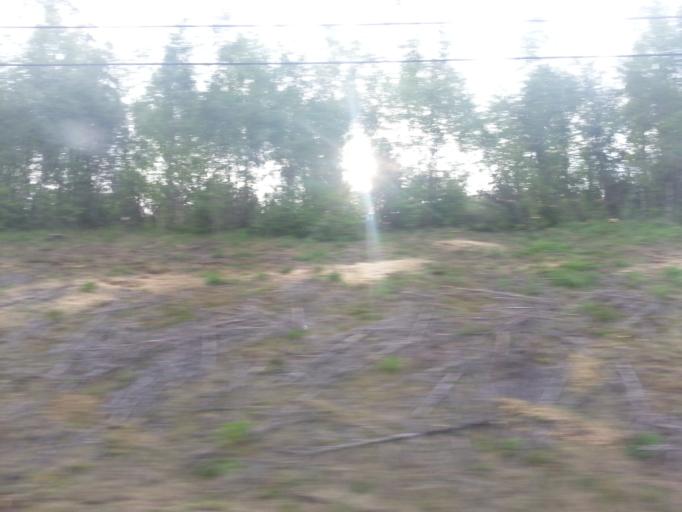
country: NO
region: Akershus
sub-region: Ullensaker
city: Jessheim
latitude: 60.1568
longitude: 11.1457
